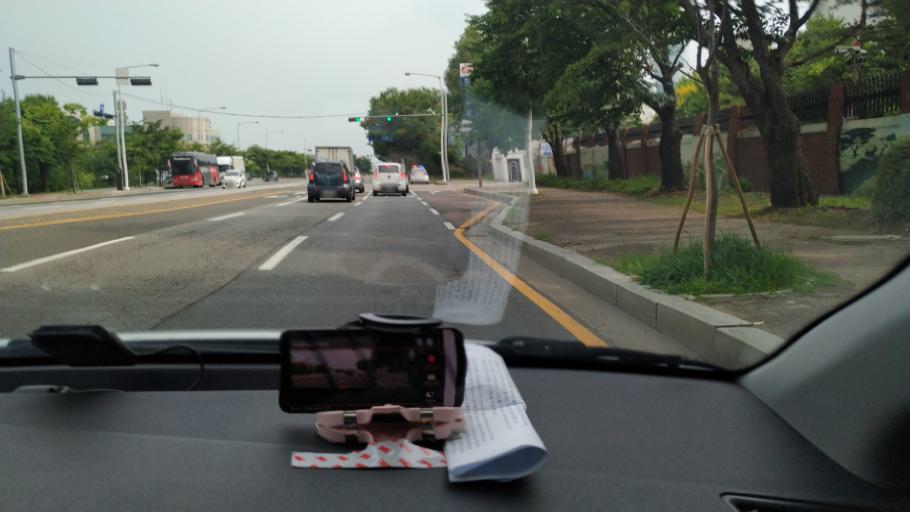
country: KR
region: Gyeonggi-do
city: Goyang-si
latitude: 37.6471
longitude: 126.8001
